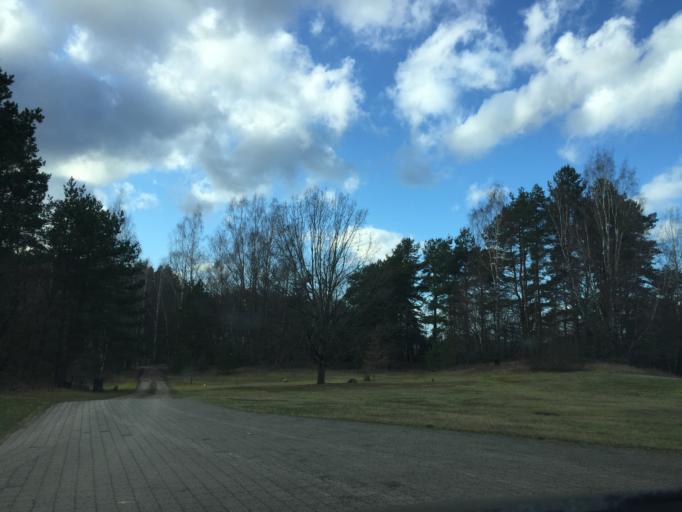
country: LV
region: Adazi
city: Adazi
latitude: 57.0577
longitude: 24.3398
